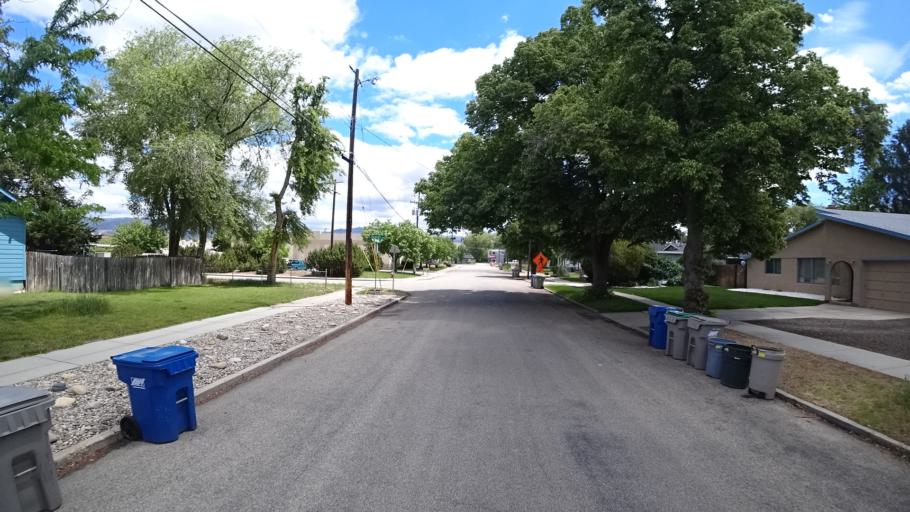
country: US
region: Idaho
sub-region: Ada County
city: Boise
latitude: 43.5837
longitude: -116.1952
